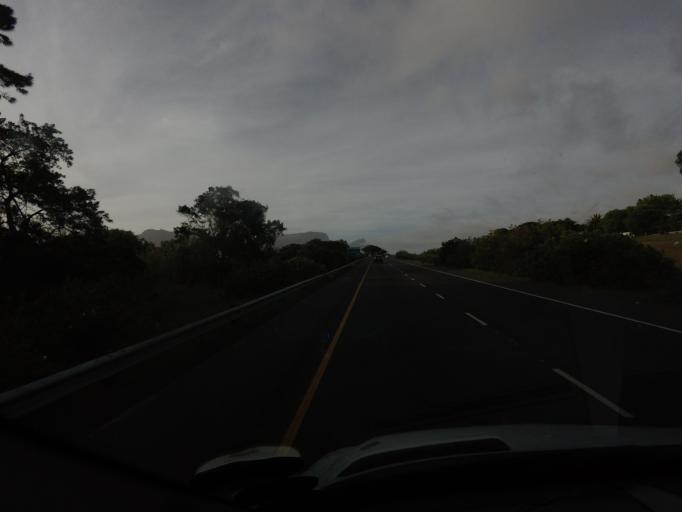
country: ZA
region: Western Cape
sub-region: City of Cape Town
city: Bergvliet
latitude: -34.0373
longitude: 18.4436
